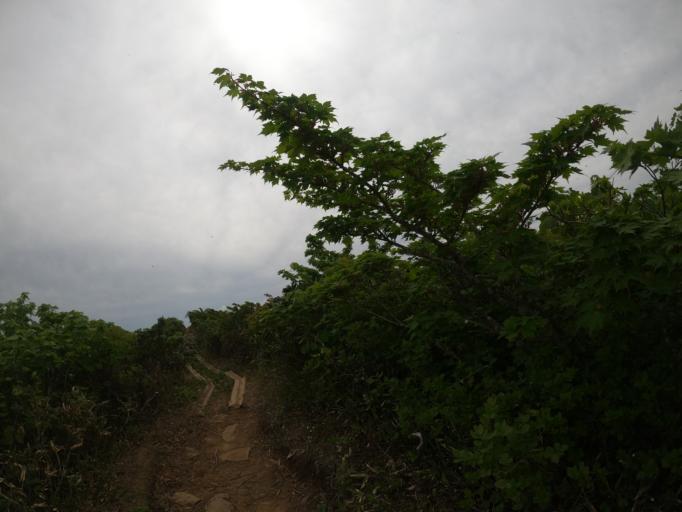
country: JP
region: Iwate
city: Ichinoseki
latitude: 38.9601
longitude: 140.7858
